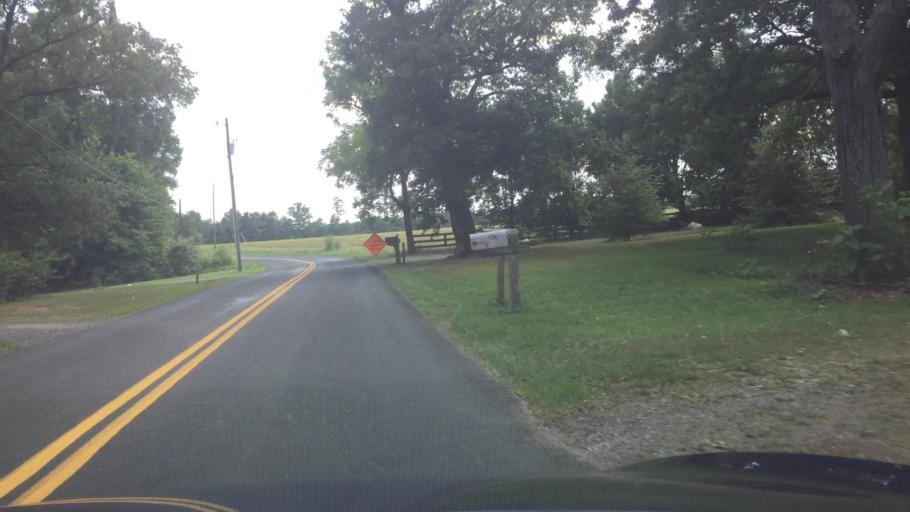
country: US
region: Virginia
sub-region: Appomattox County
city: Appomattox
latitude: 37.2862
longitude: -78.8518
